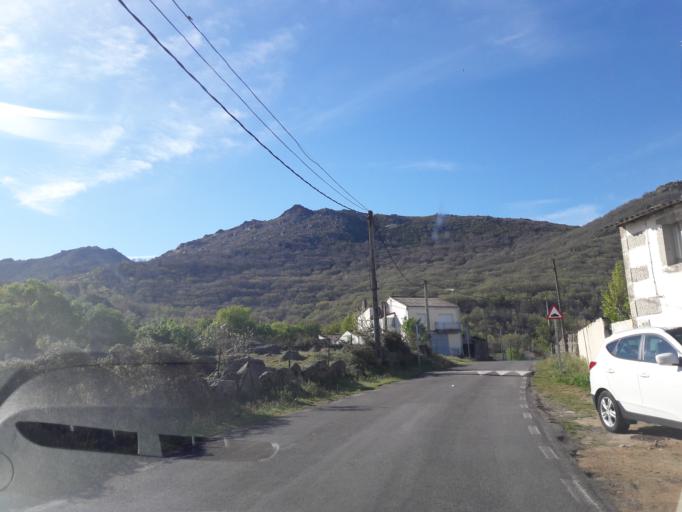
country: ES
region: Castille and Leon
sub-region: Provincia de Salamanca
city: Sanchotello
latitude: 40.4380
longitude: -5.7522
